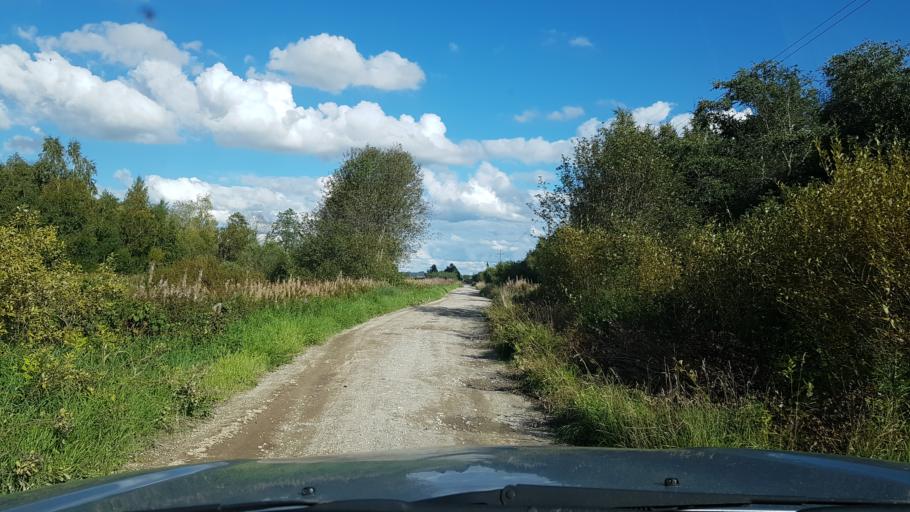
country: EE
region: Harju
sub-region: Kiili vald
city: Kiili
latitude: 59.3566
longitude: 24.8173
